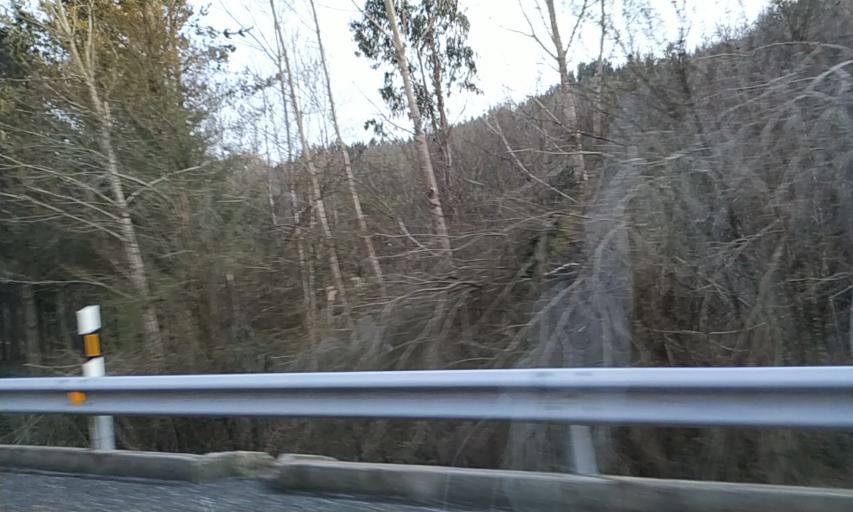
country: ES
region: Galicia
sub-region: Provincia de Lugo
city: O Paramo
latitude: 42.9092
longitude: -7.3061
